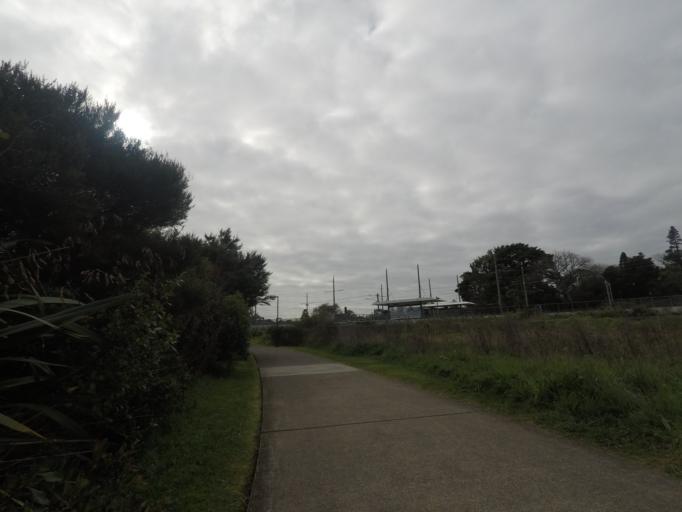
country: NZ
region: Auckland
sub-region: Auckland
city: Waitakere
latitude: -36.8971
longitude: 174.6312
